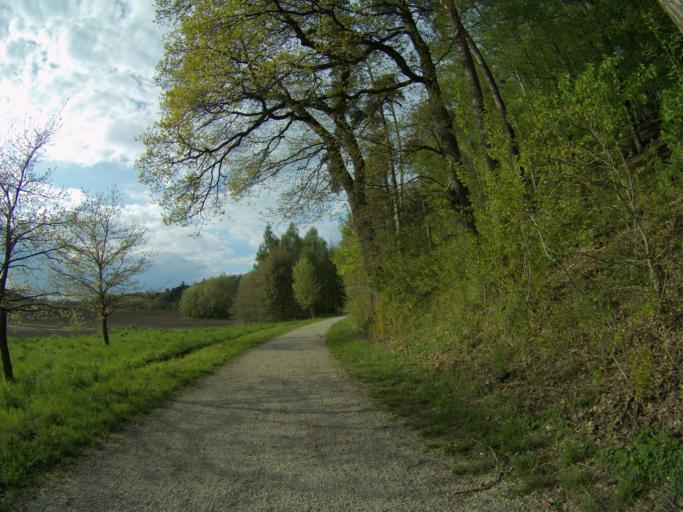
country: DE
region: Bavaria
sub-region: Upper Bavaria
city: Freising
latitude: 48.4151
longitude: 11.7551
